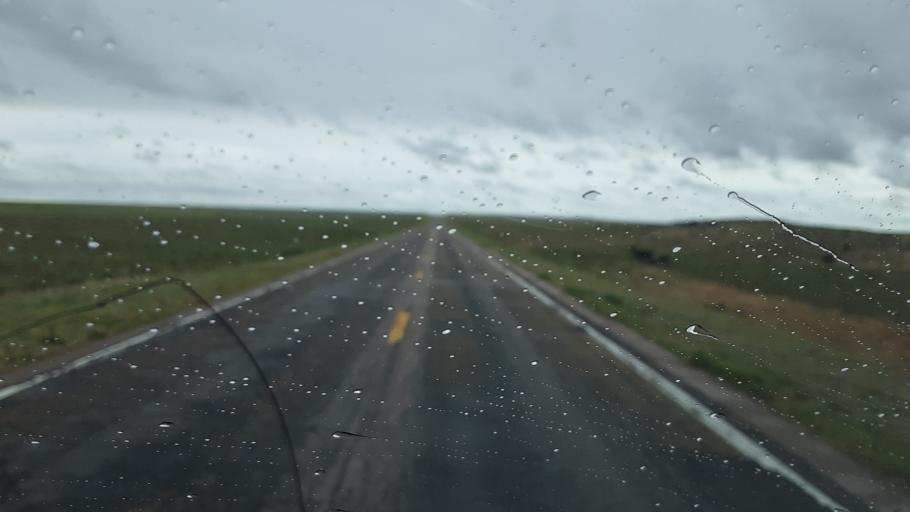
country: US
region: Colorado
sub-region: Lincoln County
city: Hugo
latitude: 38.8495
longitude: -103.2929
